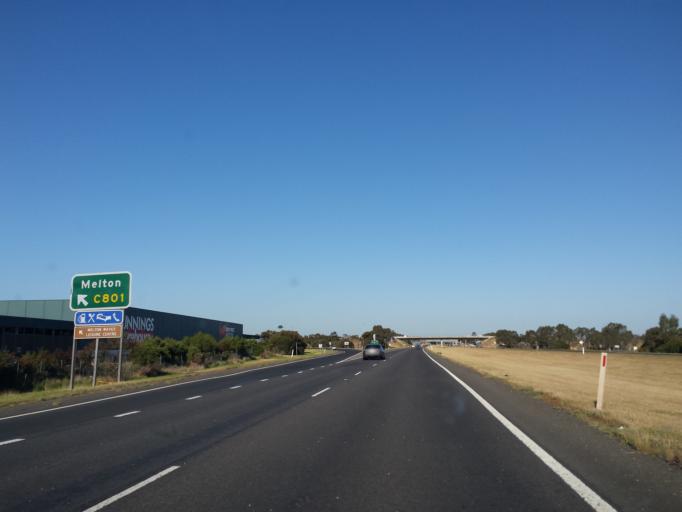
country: AU
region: Victoria
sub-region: Melton
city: Brookfield
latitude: -37.6894
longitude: 144.5611
